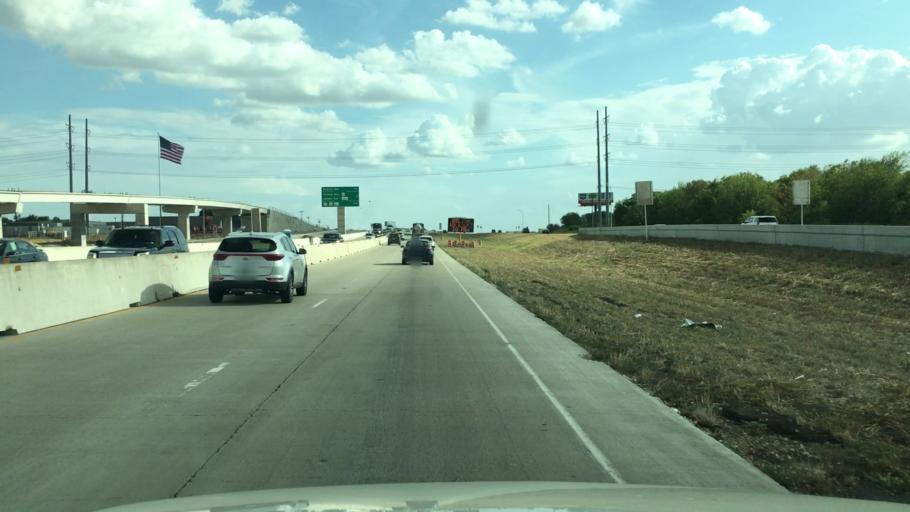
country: US
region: Texas
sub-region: Bell County
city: Temple
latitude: 31.1336
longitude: -97.3322
